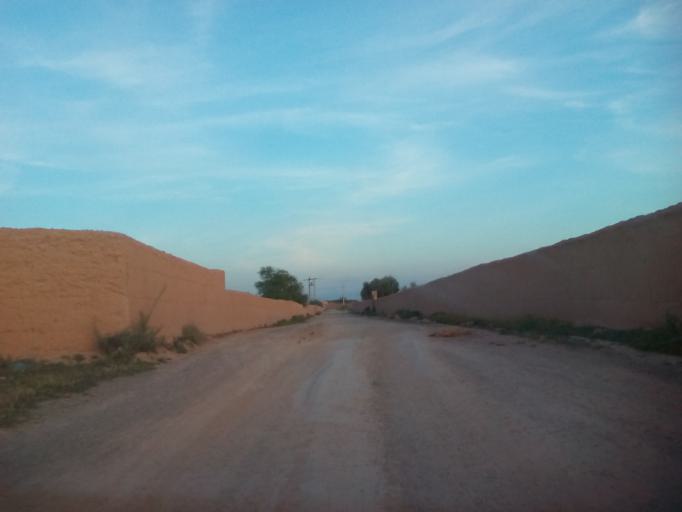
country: MA
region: Marrakech-Tensift-Al Haouz
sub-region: Marrakech
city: Marrakesh
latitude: 31.6270
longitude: -8.2862
